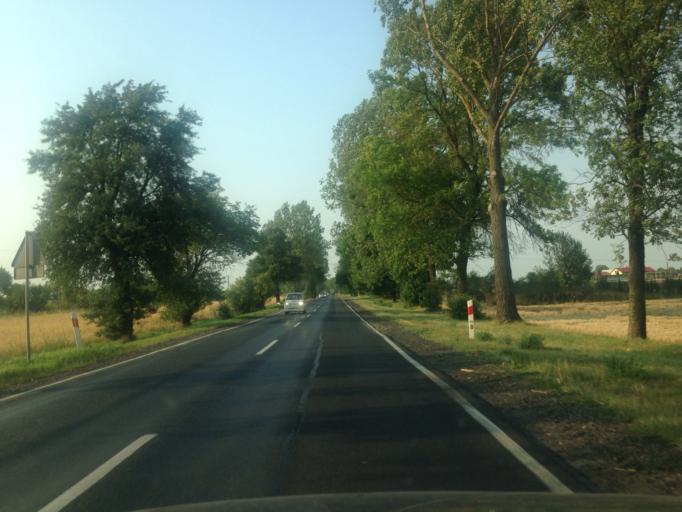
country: PL
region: Kujawsko-Pomorskie
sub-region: Powiat wloclawski
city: Fabianki
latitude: 52.7449
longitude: 19.1055
